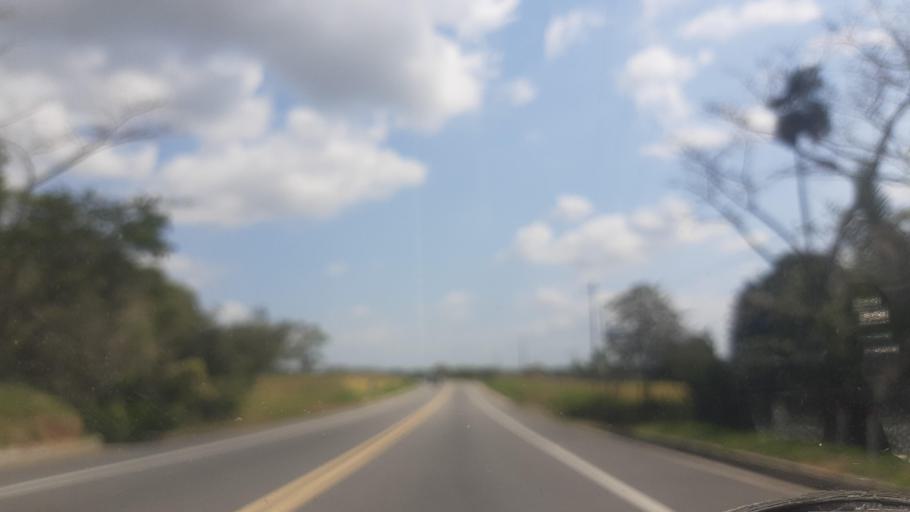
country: CO
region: Casanare
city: Tauramena
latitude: 4.8455
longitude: -72.7259
